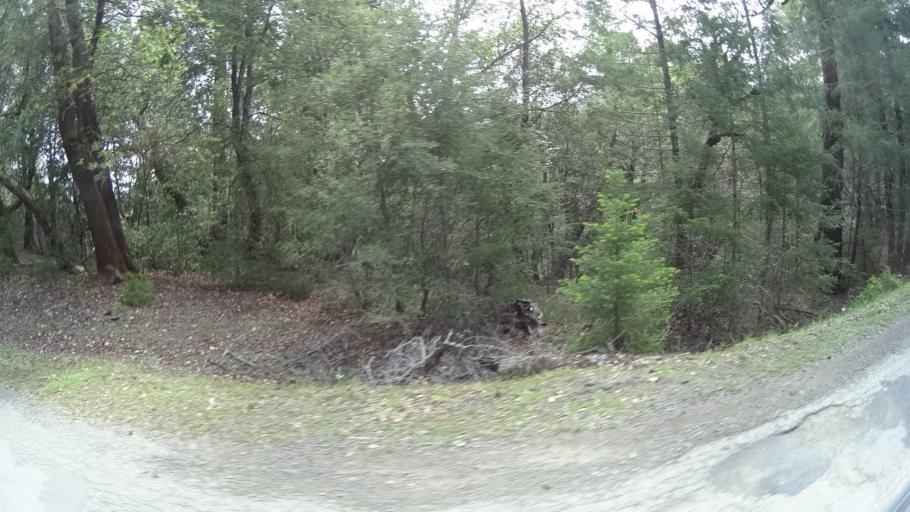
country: US
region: California
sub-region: Humboldt County
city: Redway
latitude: 40.0595
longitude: -123.8322
